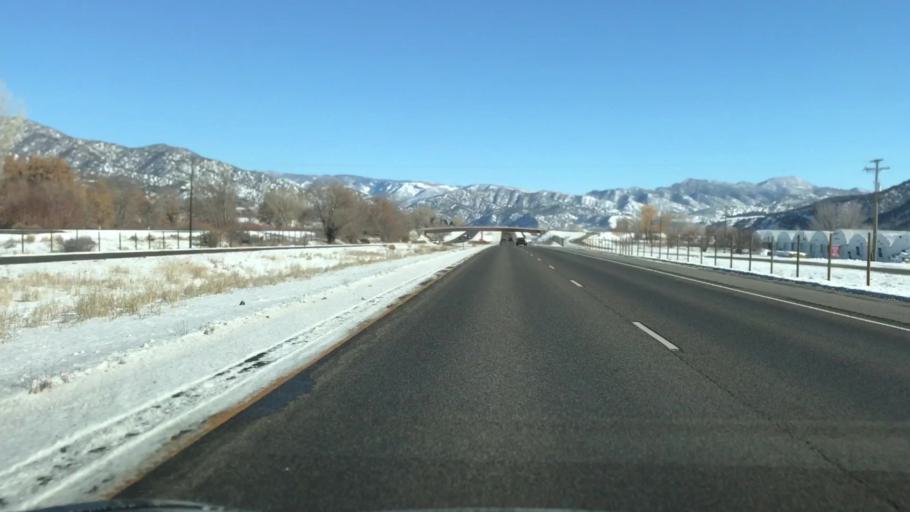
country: US
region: Colorado
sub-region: Garfield County
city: Silt
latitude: 39.5505
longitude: -107.5985
